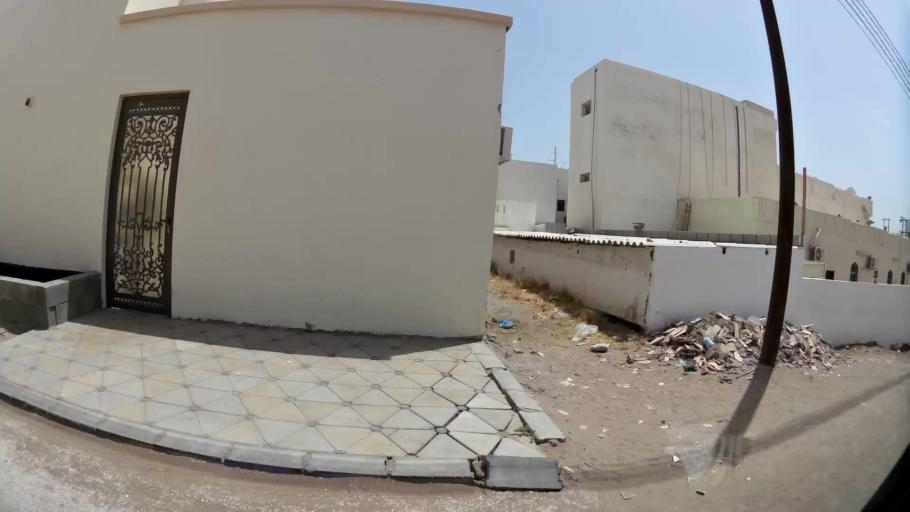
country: OM
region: Muhafazat Masqat
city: Bawshar
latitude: 23.5916
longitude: 58.4374
